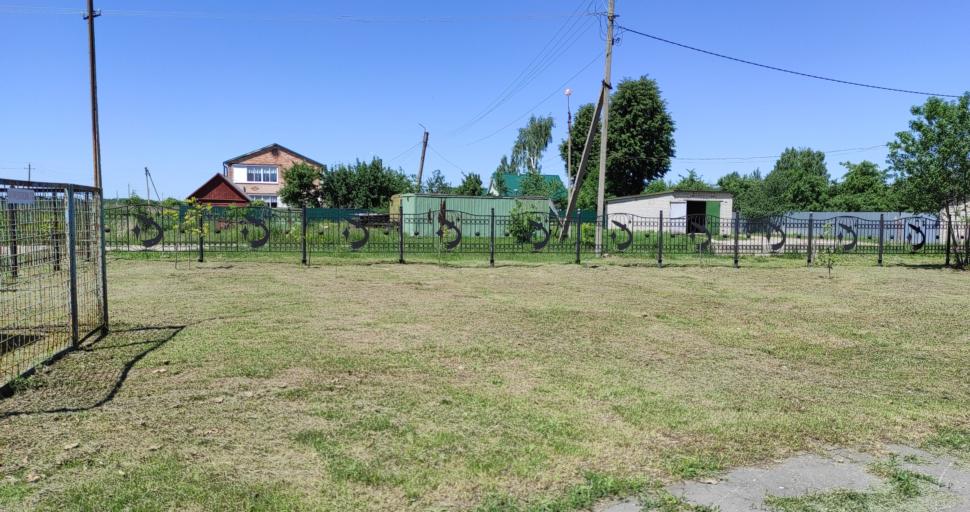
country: RU
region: Rjazan
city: Izhevskoye
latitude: 54.5494
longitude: 40.8530
